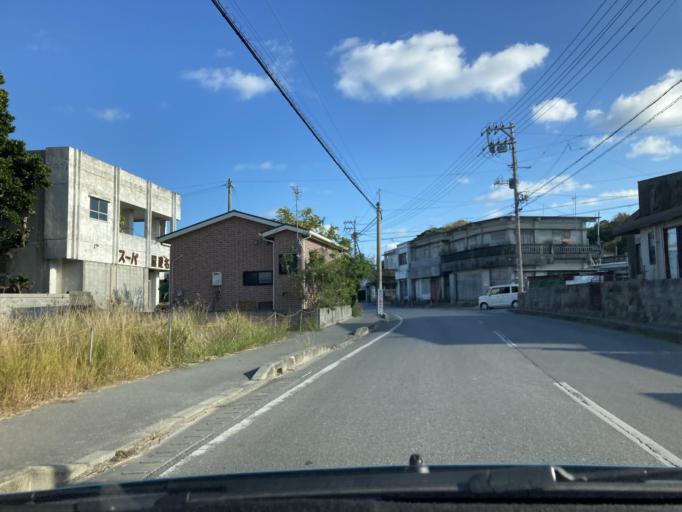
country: JP
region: Okinawa
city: Katsuren-haebaru
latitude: 26.3242
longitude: 127.9062
